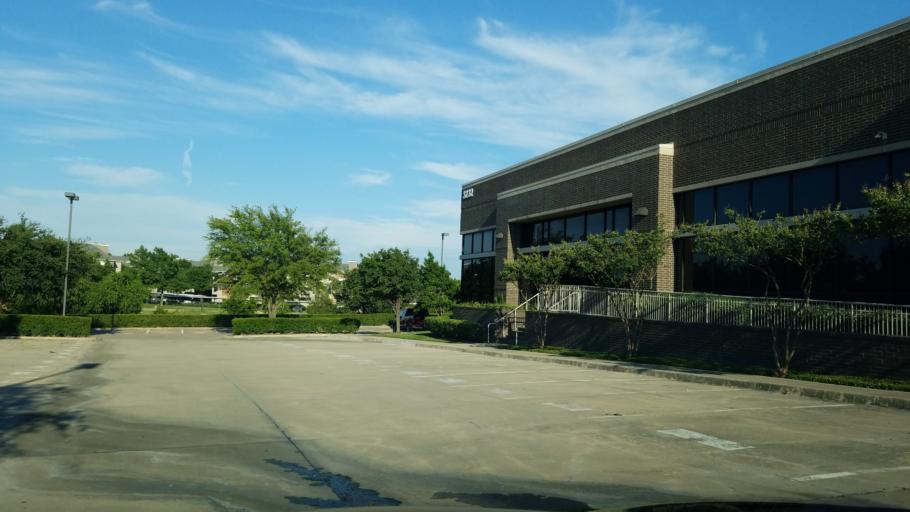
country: US
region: Texas
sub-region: Dallas County
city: Coppell
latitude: 32.9102
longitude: -96.9895
